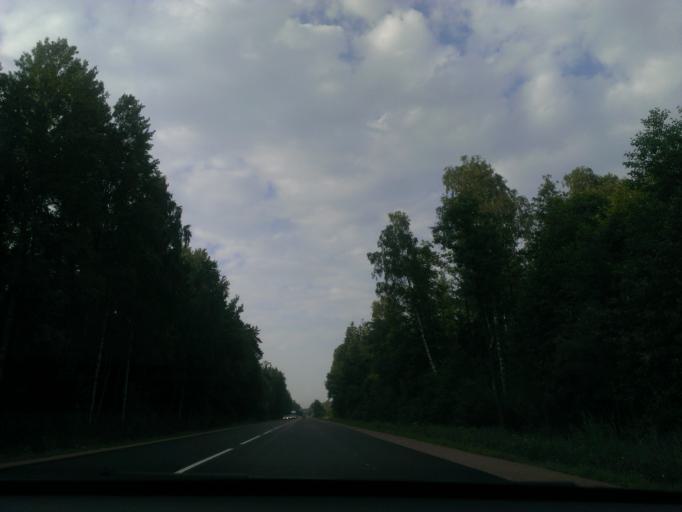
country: LV
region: Lecava
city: Iecava
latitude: 56.6955
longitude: 24.2424
